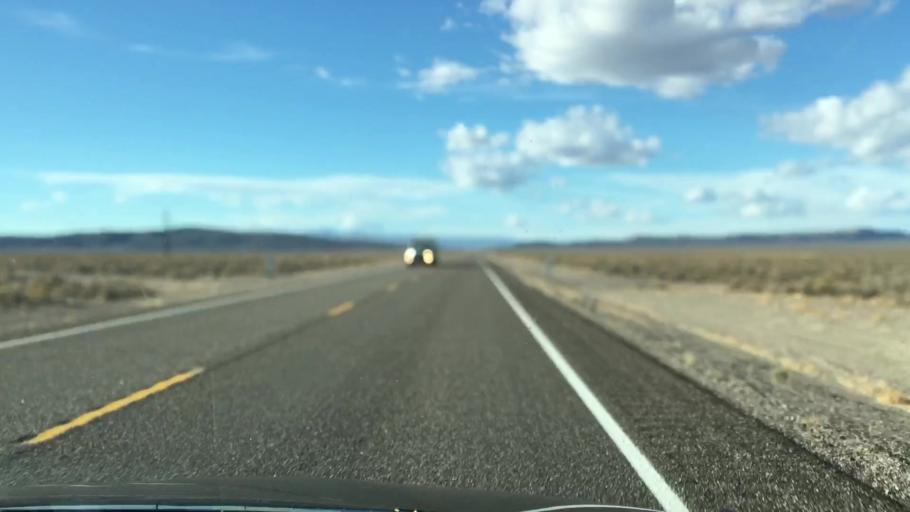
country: US
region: Nevada
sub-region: Nye County
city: Beatty
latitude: 37.1333
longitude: -116.8464
